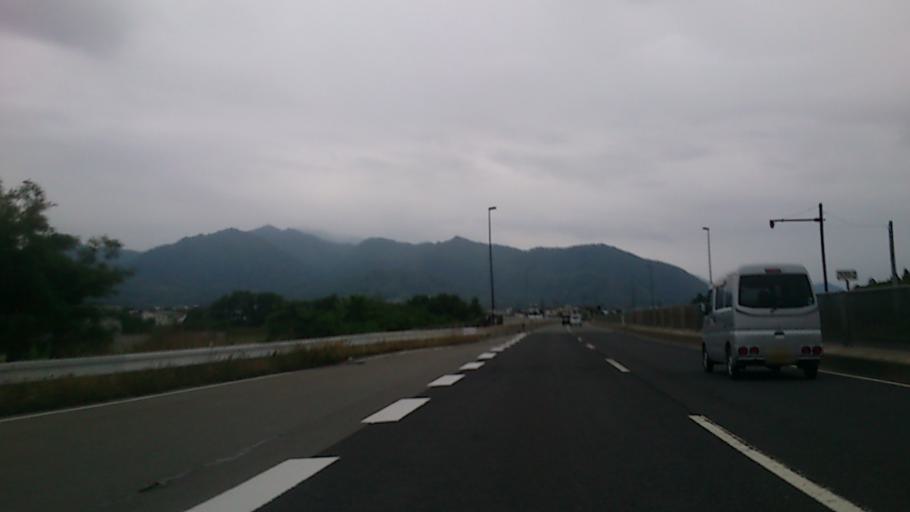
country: JP
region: Yamagata
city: Tendo
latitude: 38.3948
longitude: 140.3779
